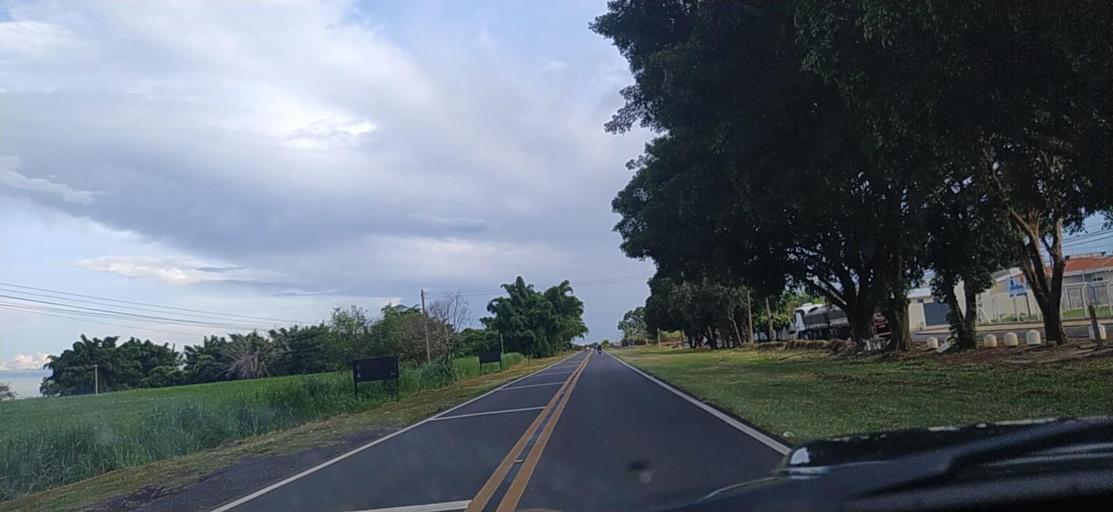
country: BR
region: Sao Paulo
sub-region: Pindorama
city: Pindorama
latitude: -21.1743
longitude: -48.9229
